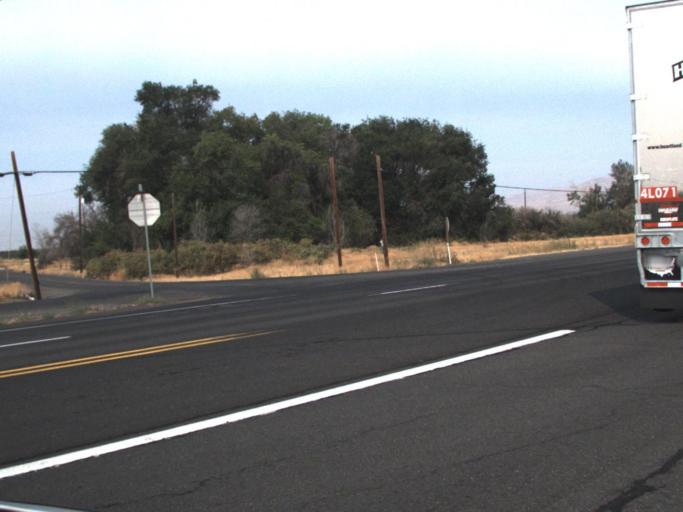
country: US
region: Washington
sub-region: Yakima County
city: Wapato
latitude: 46.4773
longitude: -120.4466
